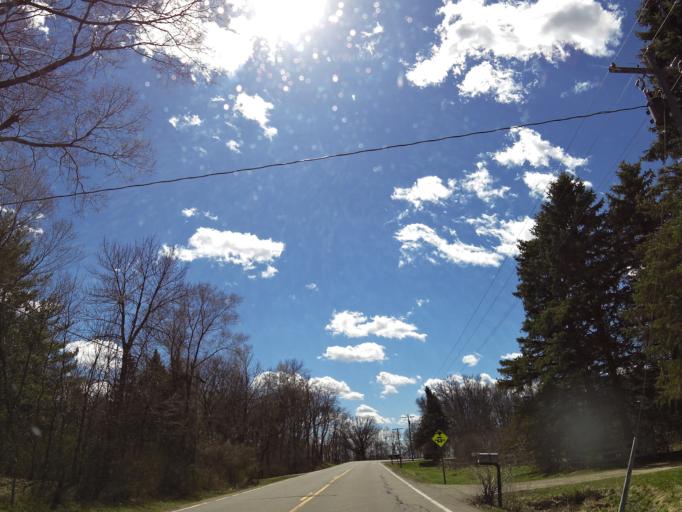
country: US
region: Minnesota
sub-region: Washington County
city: Cottage Grove
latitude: 44.7481
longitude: -92.9359
